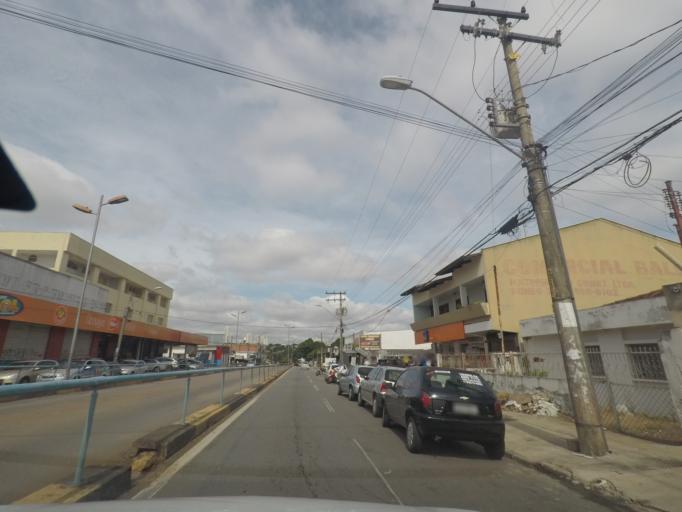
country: BR
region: Goias
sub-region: Goiania
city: Goiania
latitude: -16.6690
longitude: -49.2185
